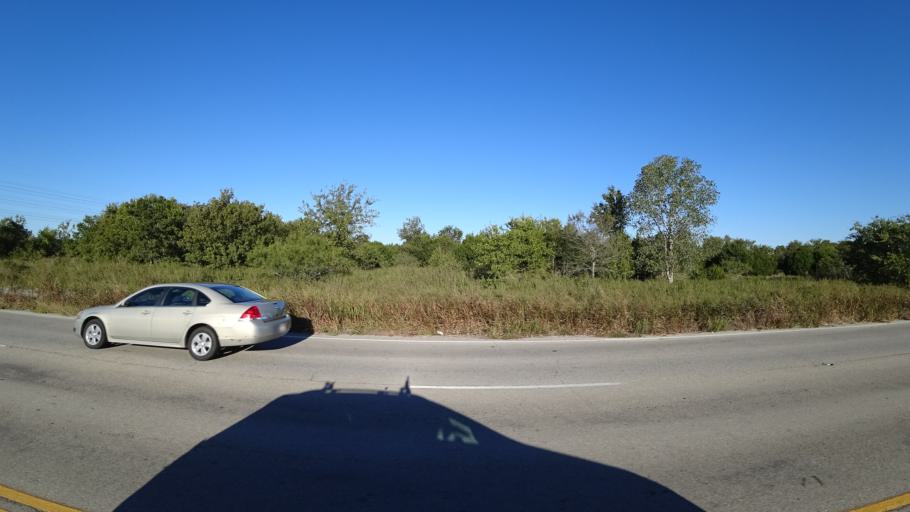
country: US
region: Texas
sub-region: Travis County
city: Manor
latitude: 30.3154
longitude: -97.6348
